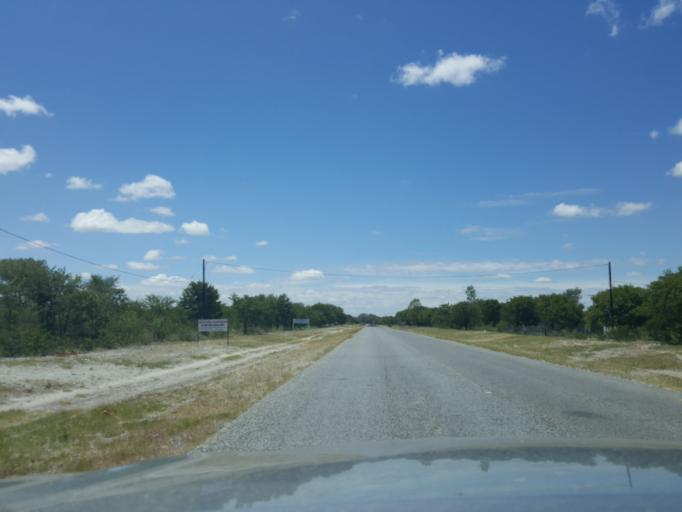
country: BW
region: Central
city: Nata
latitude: -20.2135
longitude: 26.1693
